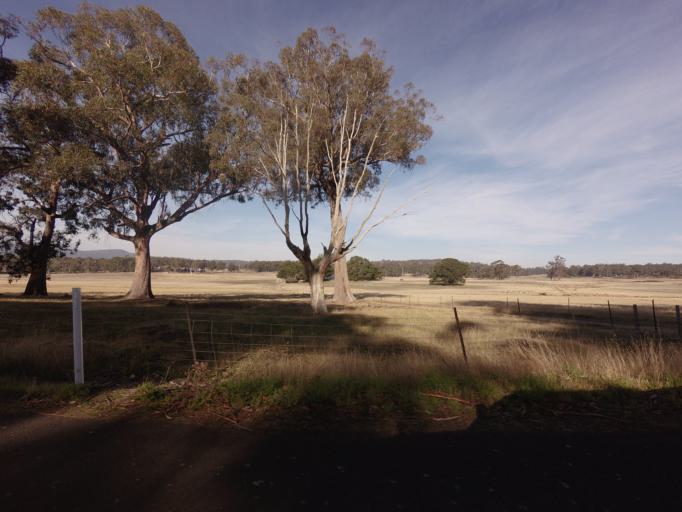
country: AU
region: Tasmania
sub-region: Sorell
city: Sorell
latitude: -42.4740
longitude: 147.4603
